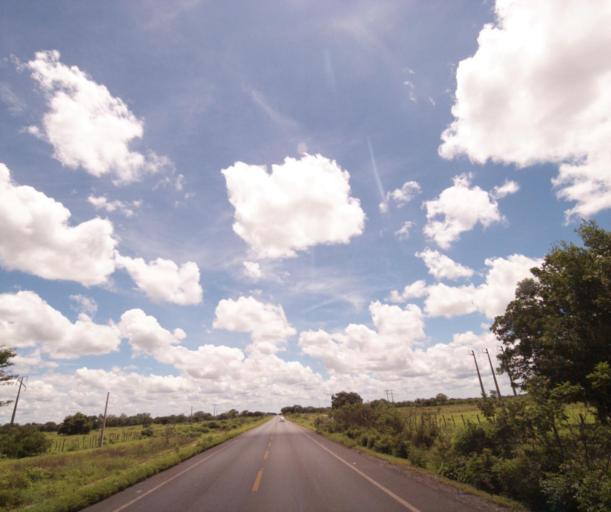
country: BR
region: Bahia
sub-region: Bom Jesus Da Lapa
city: Bom Jesus da Lapa
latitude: -13.2610
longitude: -43.5150
